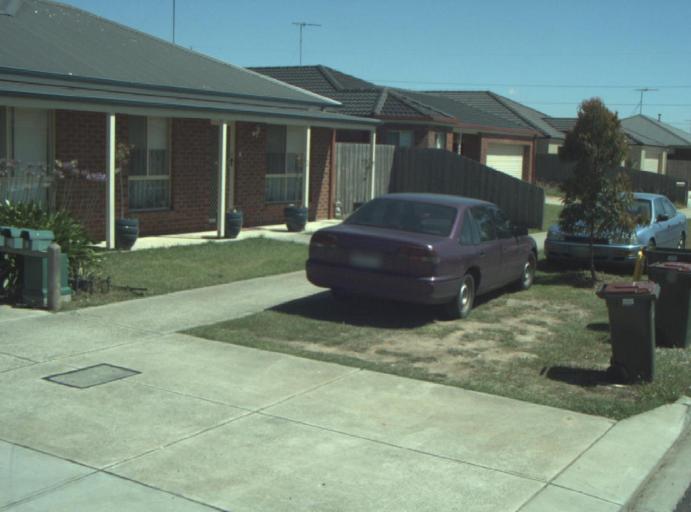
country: AU
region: Victoria
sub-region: Greater Geelong
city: Breakwater
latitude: -38.2011
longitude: 144.3469
